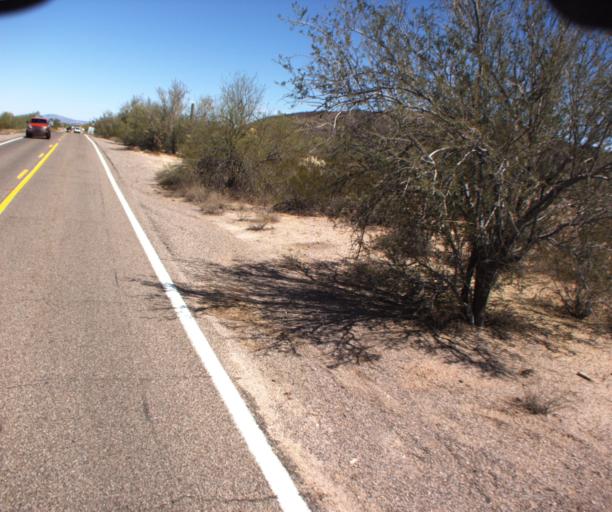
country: US
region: Arizona
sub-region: Pima County
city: Ajo
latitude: 32.1946
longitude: -112.7601
